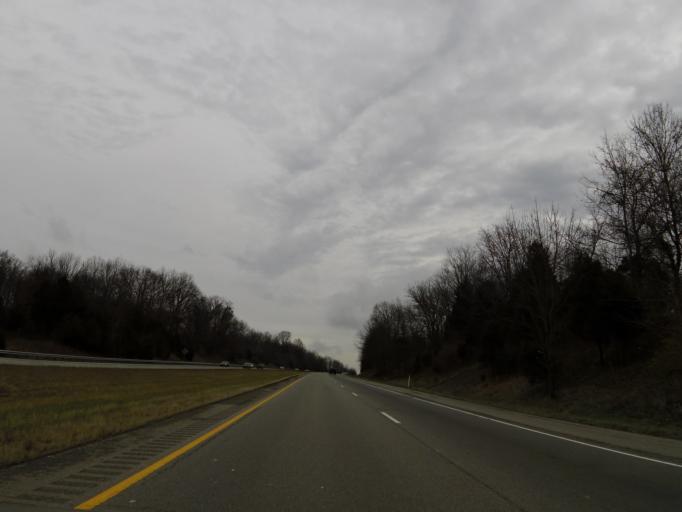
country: US
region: Indiana
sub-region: Ripley County
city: Sunman
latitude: 39.2867
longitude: -85.0069
